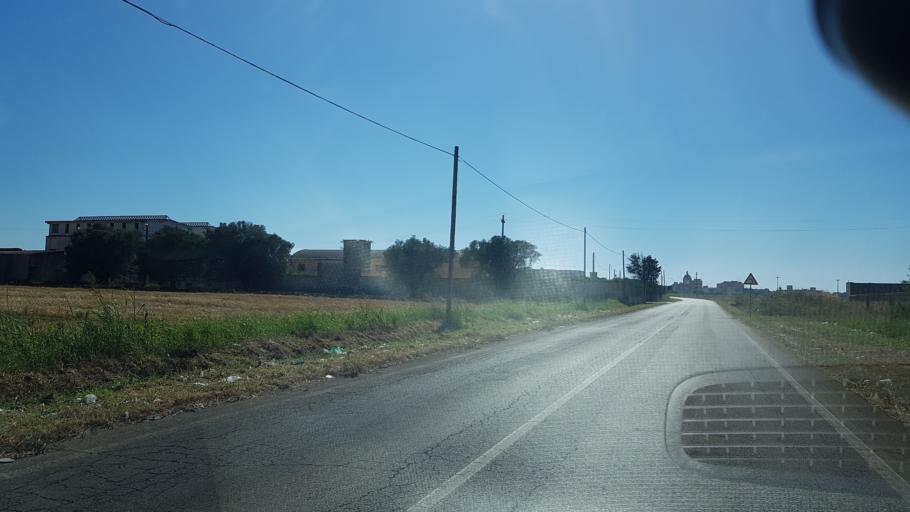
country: IT
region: Apulia
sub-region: Provincia di Brindisi
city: Mesagne
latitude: 40.5575
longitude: 17.8308
